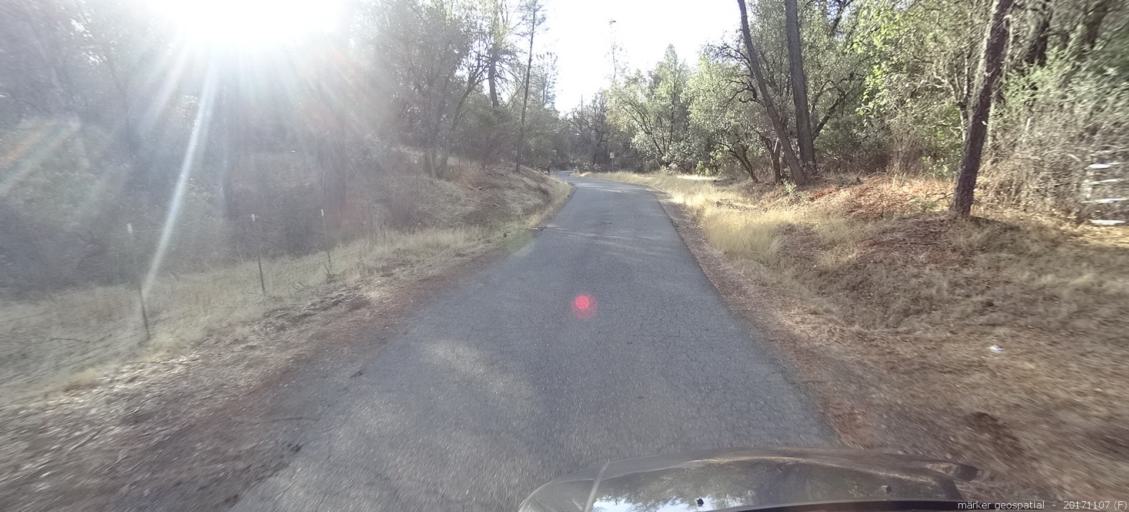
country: US
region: California
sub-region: Shasta County
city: Shasta
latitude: 40.5381
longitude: -122.4560
